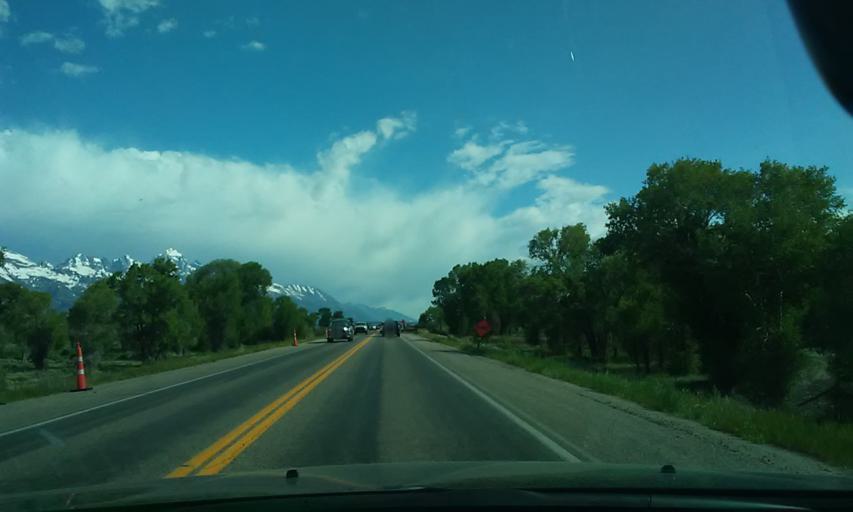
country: US
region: Wyoming
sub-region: Teton County
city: Jackson
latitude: 43.5682
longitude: -110.7331
